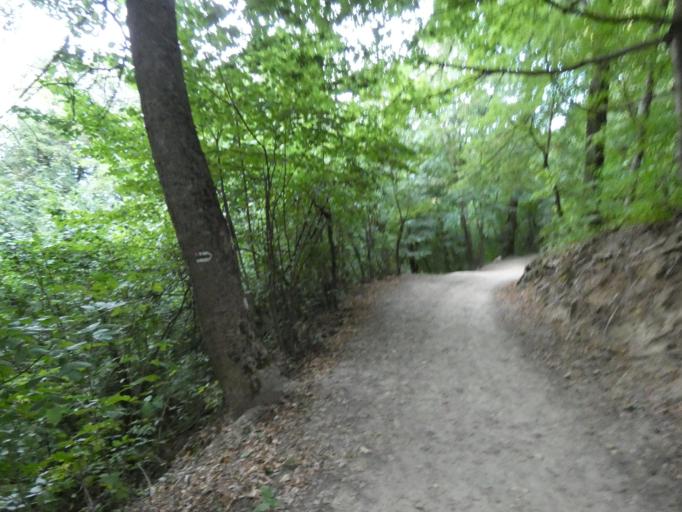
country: HU
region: Budapest
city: Budapest III. keruelet
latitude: 47.5537
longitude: 19.0045
